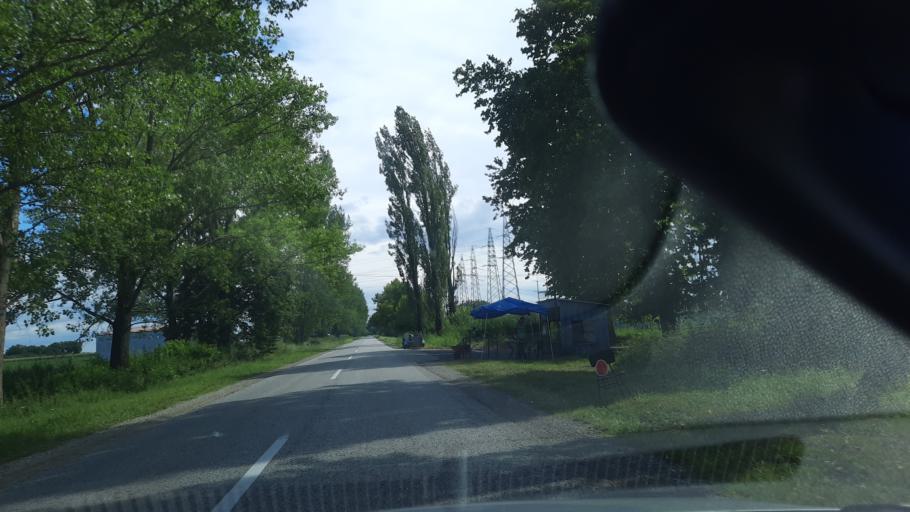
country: RS
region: Autonomna Pokrajina Vojvodina
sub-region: Sremski Okrug
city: Sremska Mitrovica
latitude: 45.0169
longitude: 19.6144
